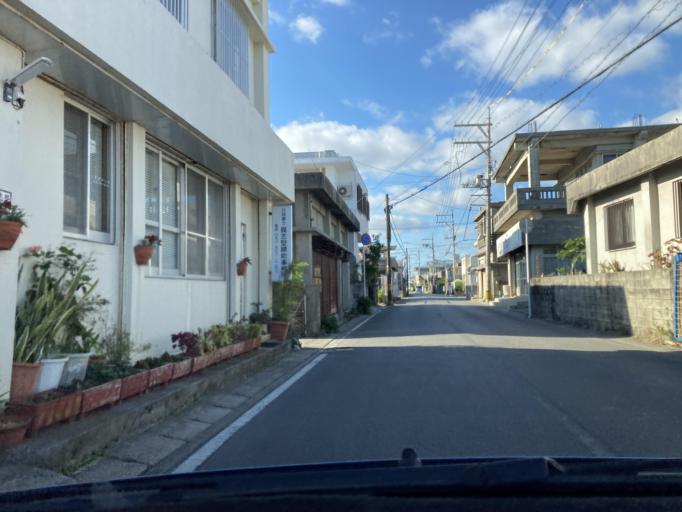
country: JP
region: Okinawa
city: Katsuren-haebaru
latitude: 26.3245
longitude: 127.9056
